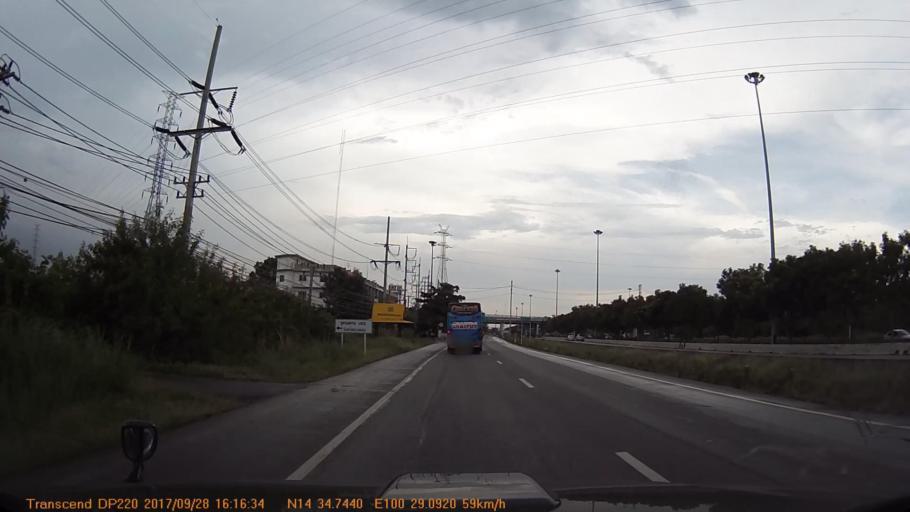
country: TH
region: Ang Thong
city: Ang Thong
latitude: 14.5794
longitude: 100.4845
